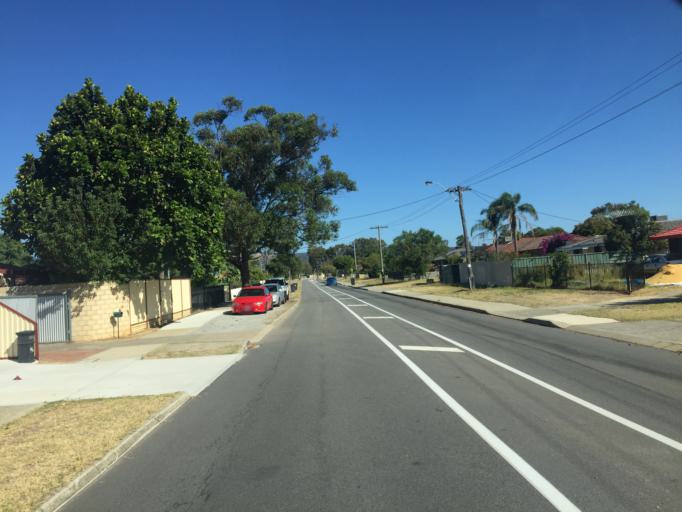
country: AU
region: Western Australia
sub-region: Gosnells
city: Maddington
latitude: -32.0490
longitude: 115.9970
